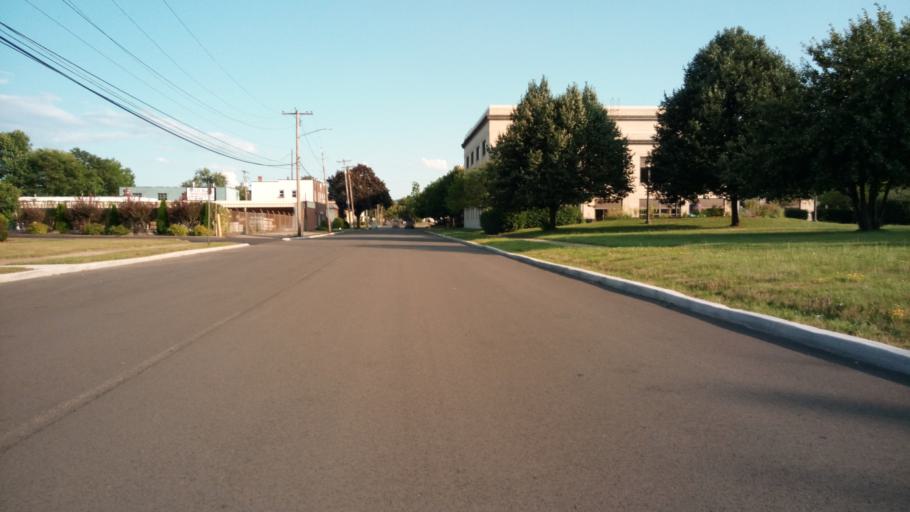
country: US
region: New York
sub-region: Chemung County
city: Elmira
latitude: 42.0975
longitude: -76.8042
